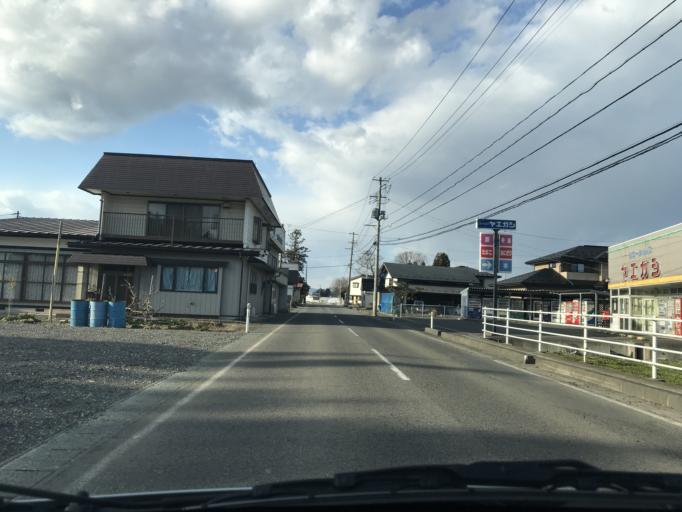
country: JP
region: Iwate
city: Kitakami
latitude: 39.3184
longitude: 141.0680
